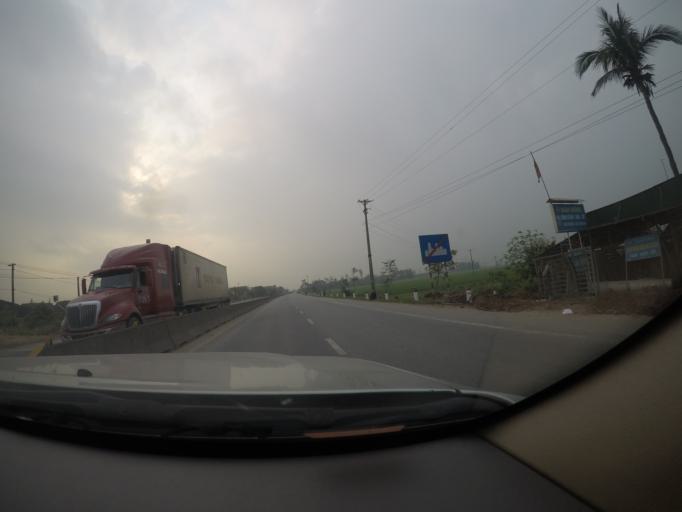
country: VN
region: Ha Tinh
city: Cam Xuyen
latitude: 18.2396
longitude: 106.0166
